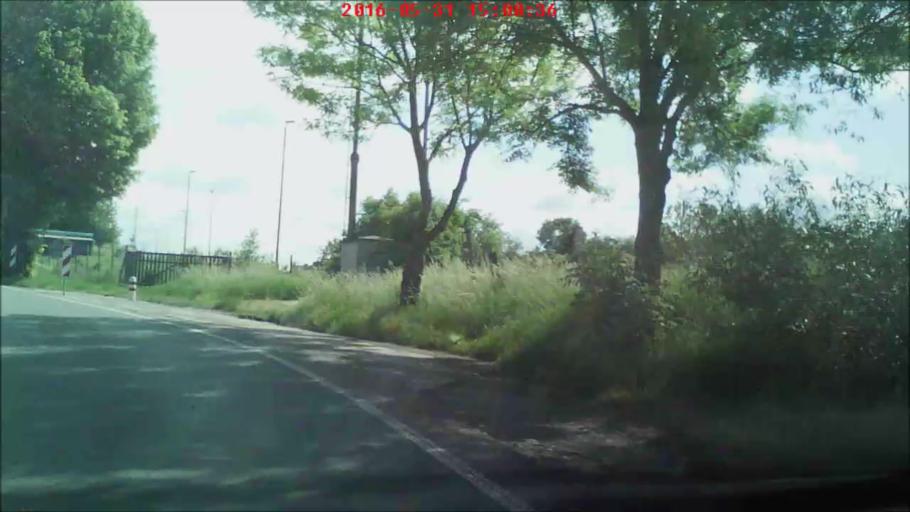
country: DE
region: Thuringia
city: Straussfurt
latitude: 51.1695
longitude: 10.9883
